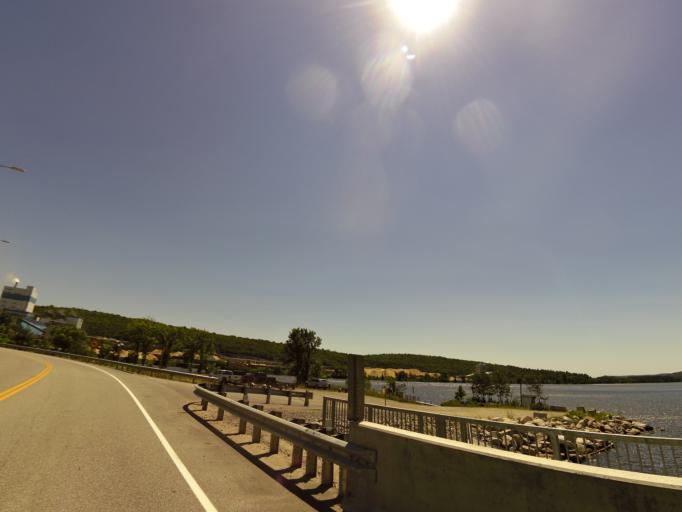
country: CA
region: Quebec
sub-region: Abitibi-Temiscamingue
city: Temiscaming
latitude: 46.7082
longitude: -79.1021
